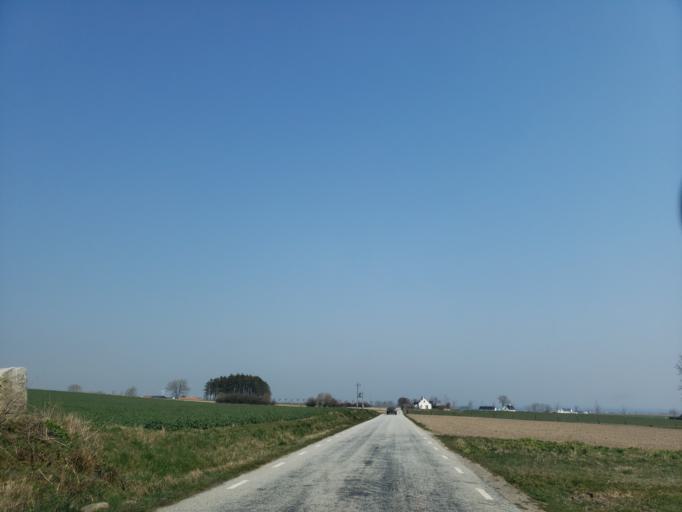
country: SE
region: Skane
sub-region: Simrishamns Kommun
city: Simrishamn
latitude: 55.5077
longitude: 14.3143
